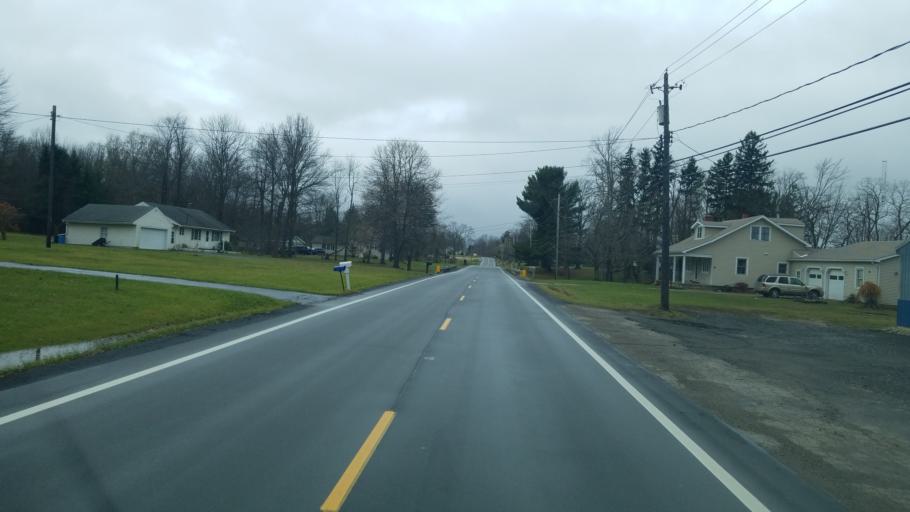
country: US
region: Ohio
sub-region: Ashtabula County
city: Edgewood
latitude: 41.8707
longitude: -80.7424
